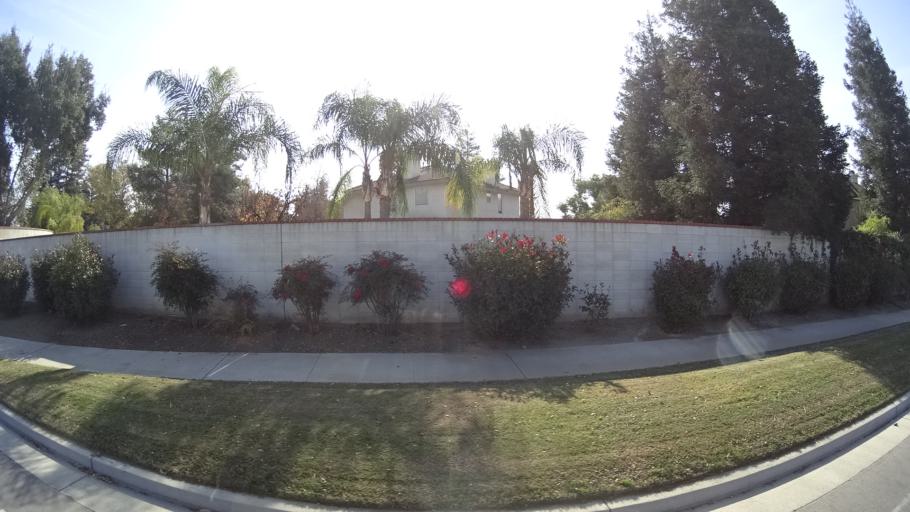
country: US
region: California
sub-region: Kern County
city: Greenacres
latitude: 35.3688
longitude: -119.1044
